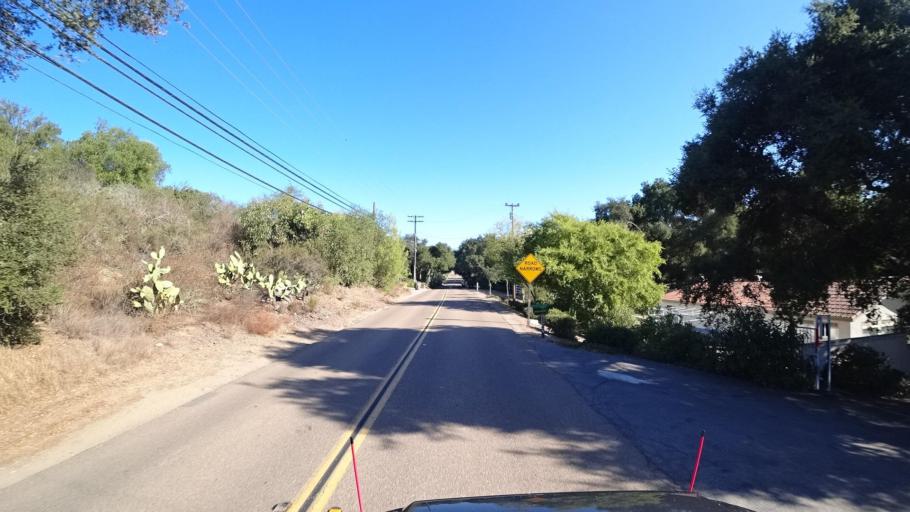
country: US
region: California
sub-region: San Diego County
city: Hidden Meadows
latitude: 33.2218
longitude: -117.1107
